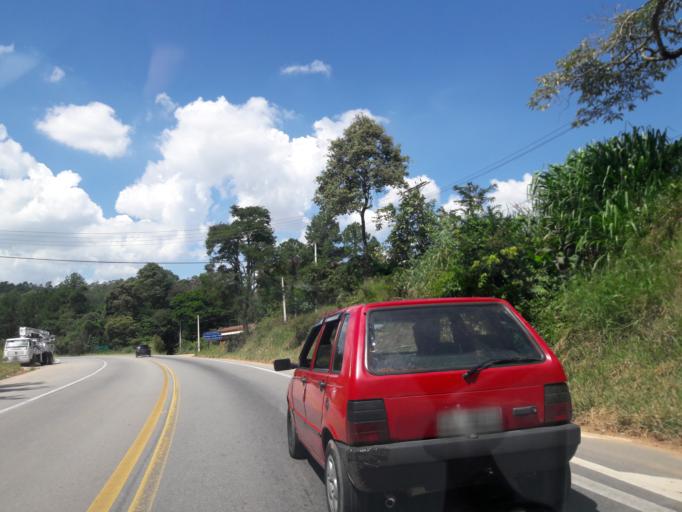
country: BR
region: Sao Paulo
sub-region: Francisco Morato
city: Francisco Morato
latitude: -23.2635
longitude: -46.7935
